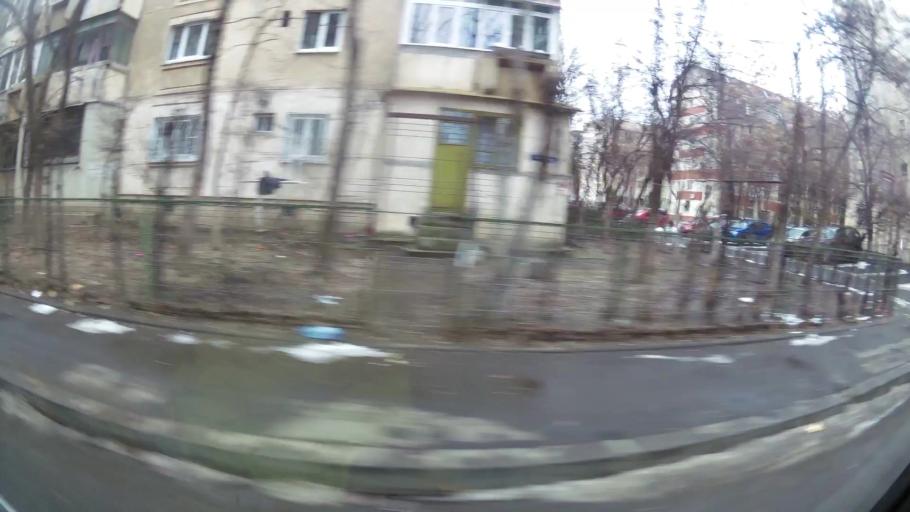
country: RO
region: Bucuresti
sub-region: Municipiul Bucuresti
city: Bucharest
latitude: 44.4161
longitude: 26.1261
